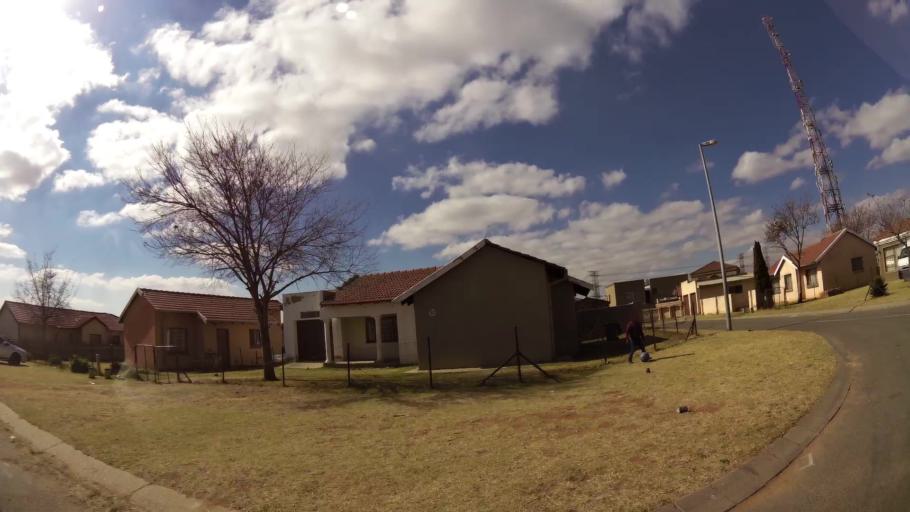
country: ZA
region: Gauteng
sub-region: City of Johannesburg Metropolitan Municipality
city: Modderfontein
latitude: -26.0315
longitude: 28.1756
